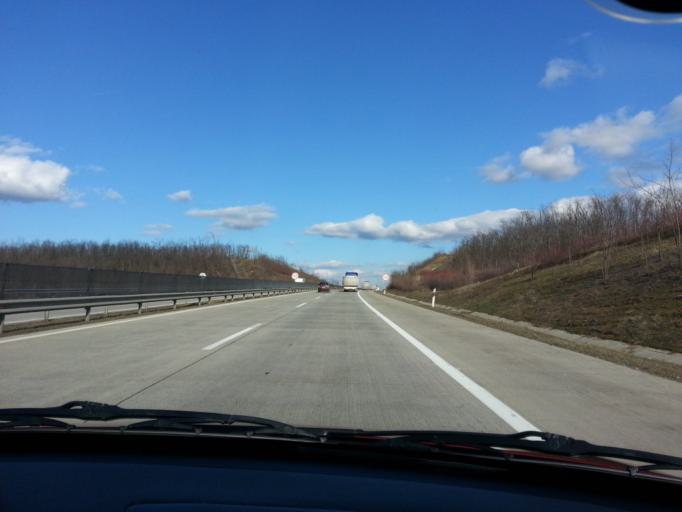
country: HU
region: Pest
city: Kerepes
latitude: 47.5612
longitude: 19.3189
